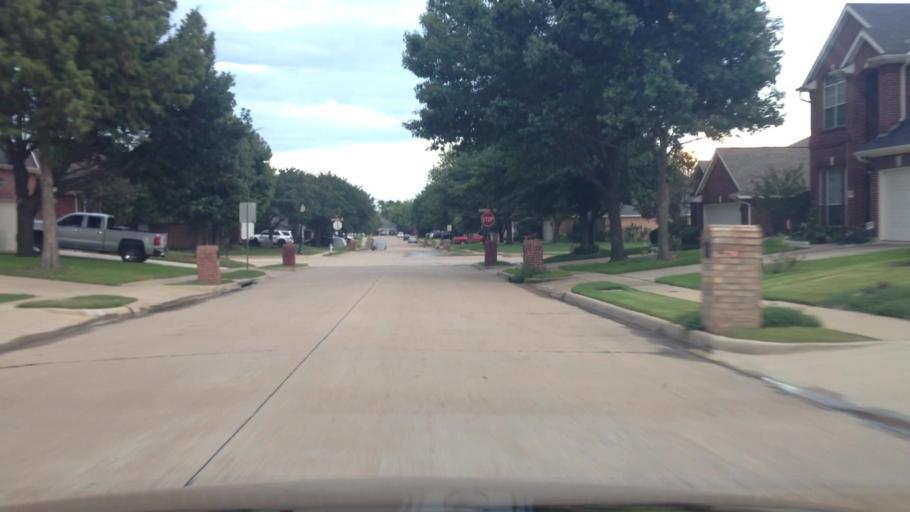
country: US
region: Texas
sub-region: Denton County
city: Flower Mound
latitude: 32.9996
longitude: -97.0551
